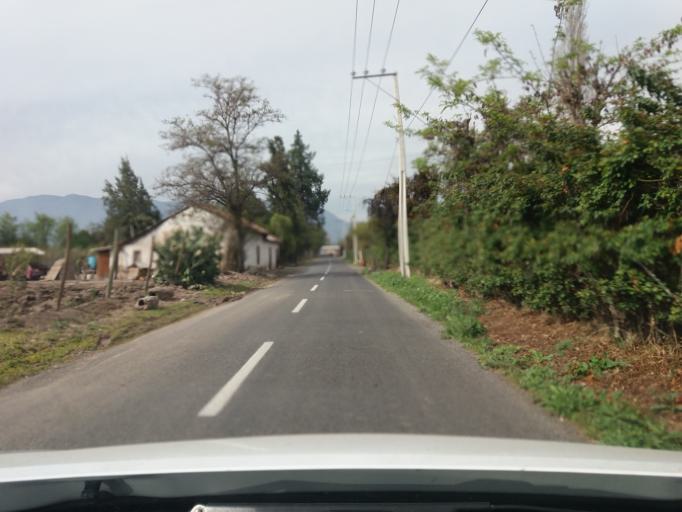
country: CL
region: Valparaiso
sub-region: Provincia de Los Andes
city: Los Andes
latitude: -32.8343
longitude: -70.6602
